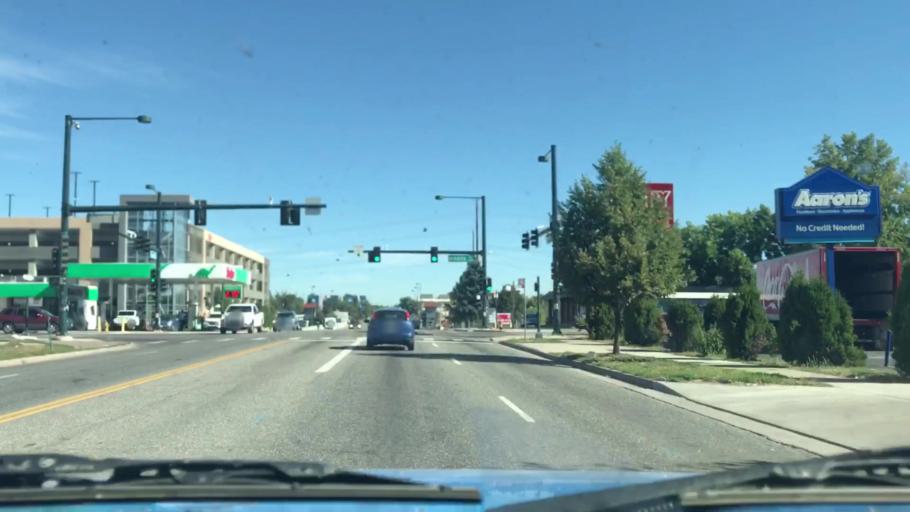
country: US
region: Colorado
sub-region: Jefferson County
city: Edgewater
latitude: 39.7325
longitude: -105.0532
